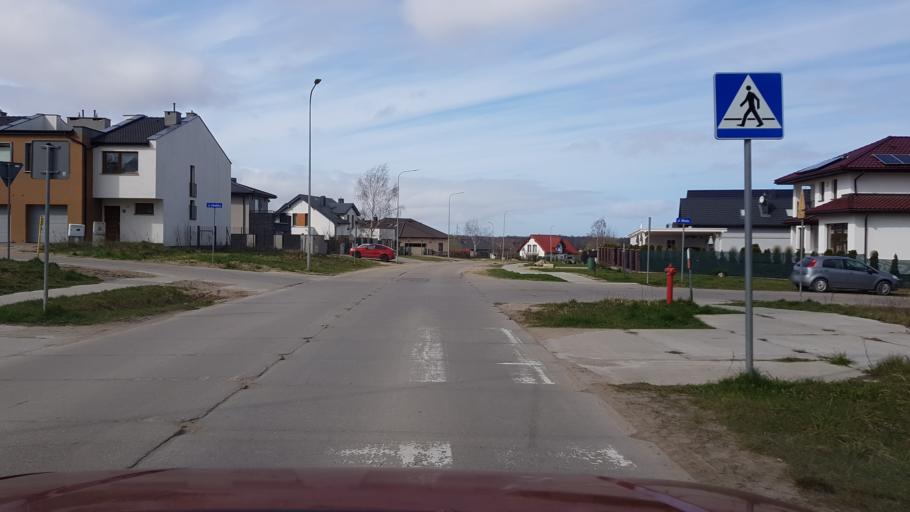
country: PL
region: West Pomeranian Voivodeship
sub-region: Koszalin
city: Koszalin
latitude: 54.2169
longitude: 16.1738
